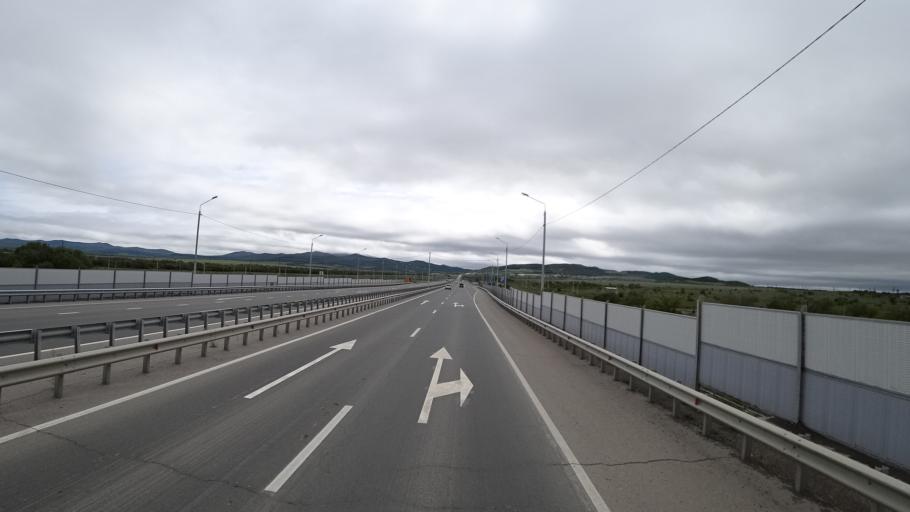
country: RU
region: Primorskiy
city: Monastyrishche
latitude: 44.1896
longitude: 132.4413
